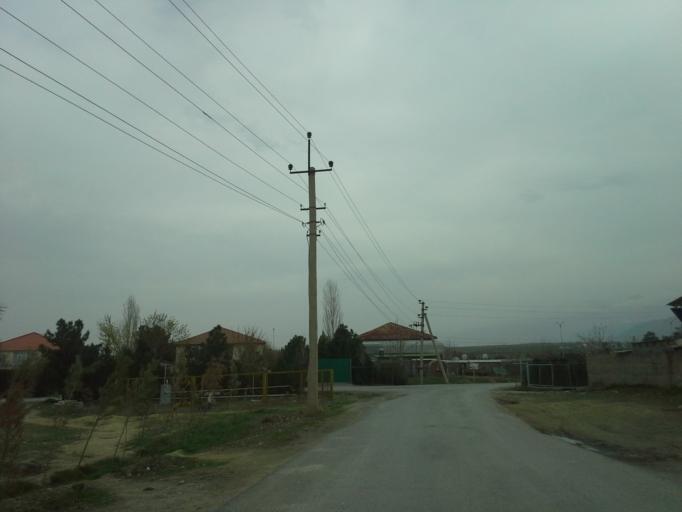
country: TM
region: Ahal
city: Abadan
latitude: 37.9709
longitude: 58.2314
